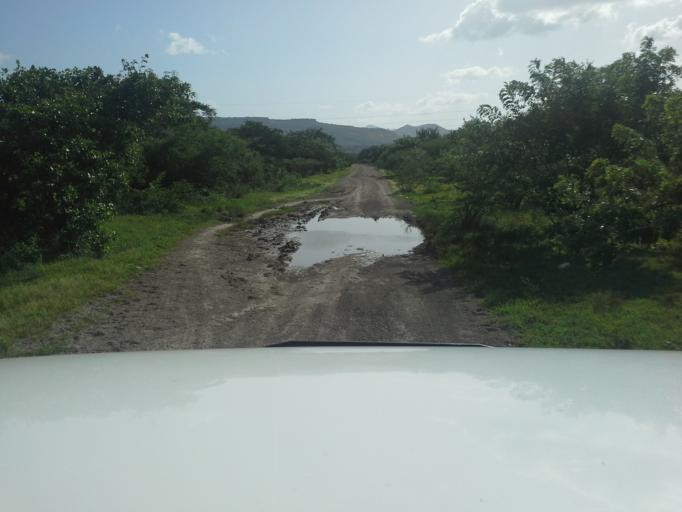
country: NI
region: Matagalpa
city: Ciudad Dario
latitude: 12.6594
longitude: -86.0744
